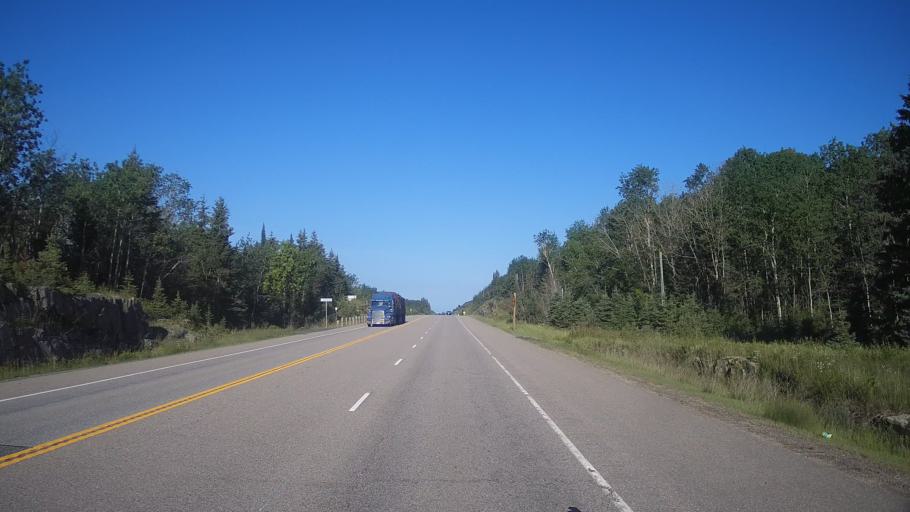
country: US
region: Minnesota
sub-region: Roseau County
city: Warroad
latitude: 49.7183
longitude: -94.7358
